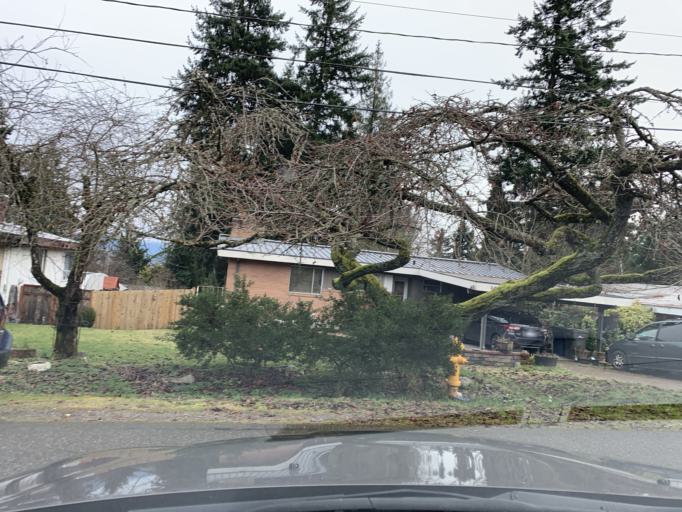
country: US
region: Washington
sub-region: King County
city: SeaTac
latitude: 47.4589
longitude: -122.2757
